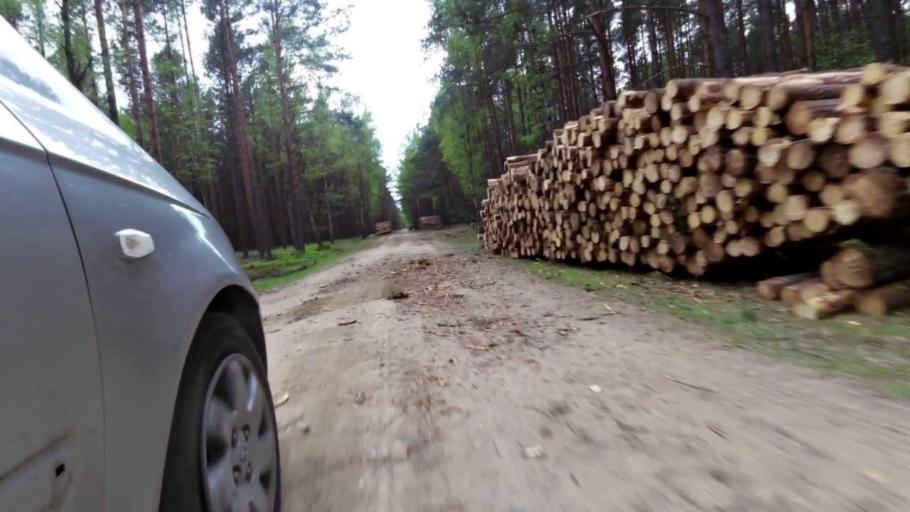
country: PL
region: West Pomeranian Voivodeship
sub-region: Powiat walecki
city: Walcz
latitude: 53.2711
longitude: 16.3850
